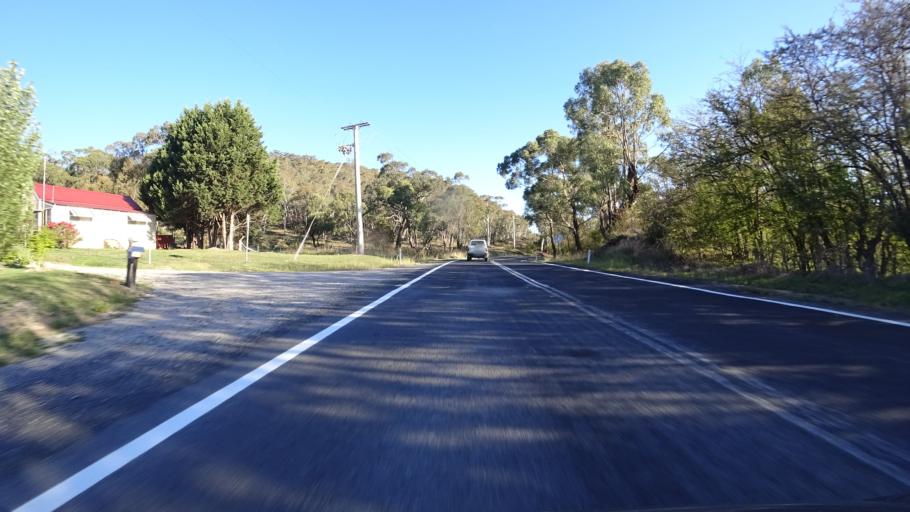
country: AU
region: New South Wales
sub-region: Lithgow
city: Portland
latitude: -33.3040
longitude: 150.0326
